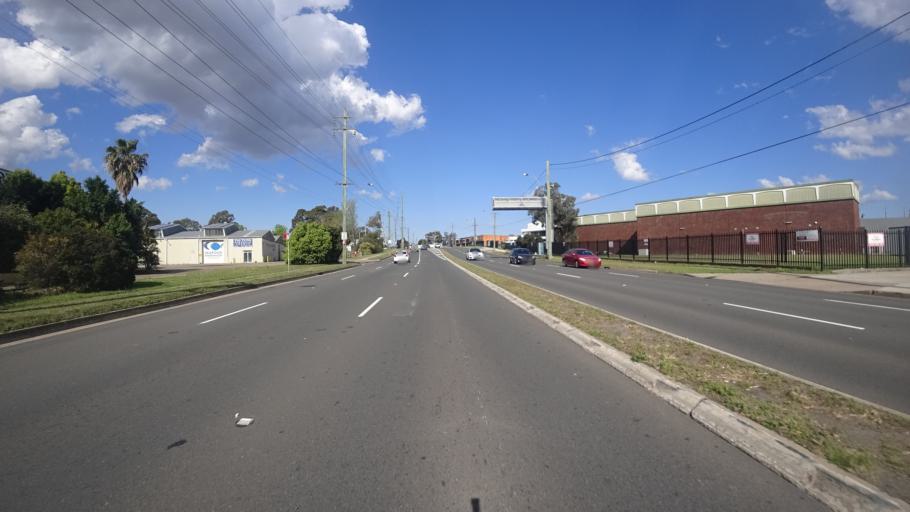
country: AU
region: New South Wales
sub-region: Fairfield
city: Liverpool
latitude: -33.9294
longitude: 150.9346
